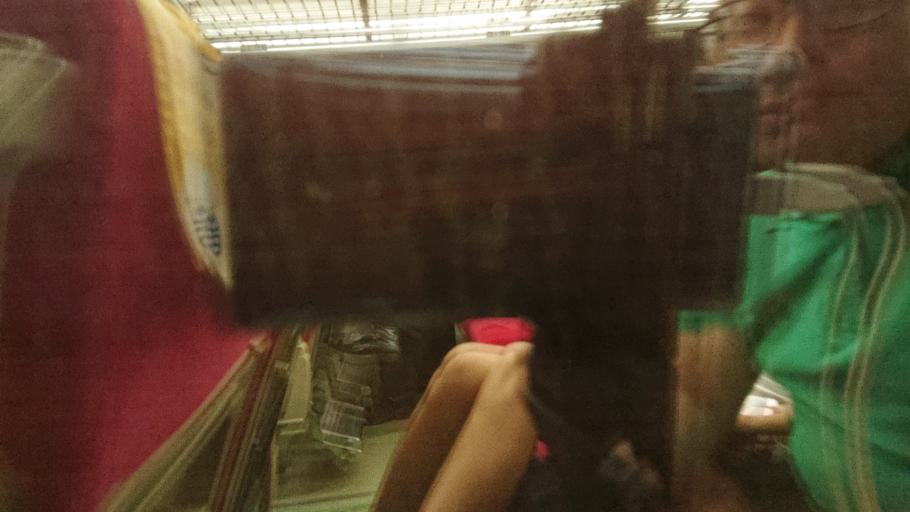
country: TW
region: Taiwan
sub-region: Keelung
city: Keelung
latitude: 25.0301
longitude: 121.8675
